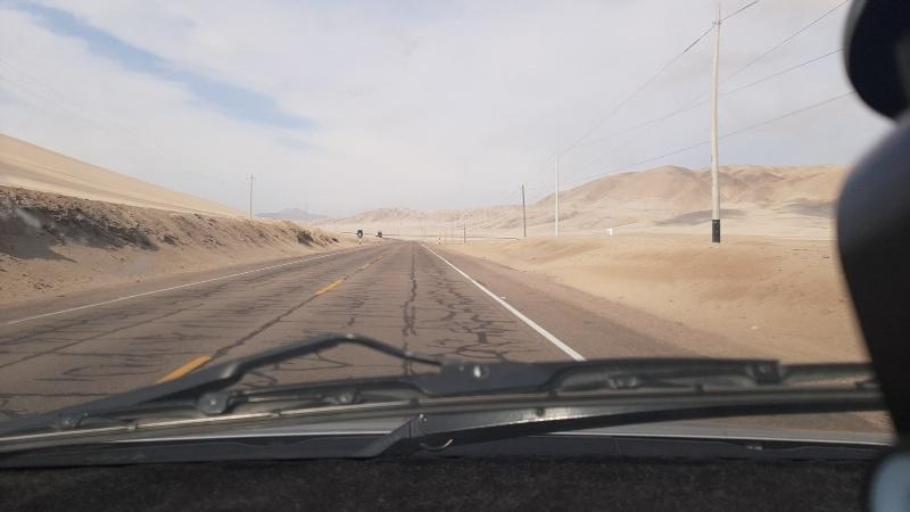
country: PE
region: Moquegua
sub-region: Provincia de Ilo
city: El Algarrobal
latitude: -17.6783
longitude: -71.2307
